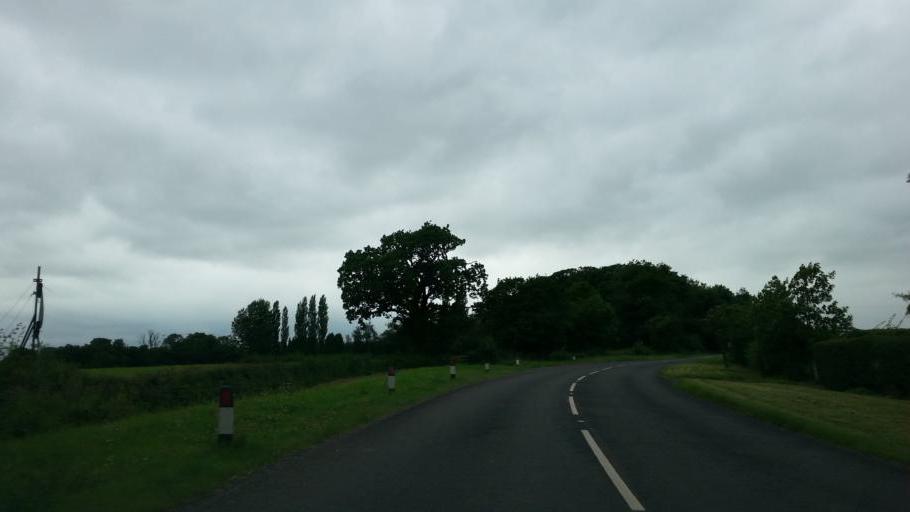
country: GB
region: England
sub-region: Nottinghamshire
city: Farnsfield
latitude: 53.0622
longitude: -1.0224
